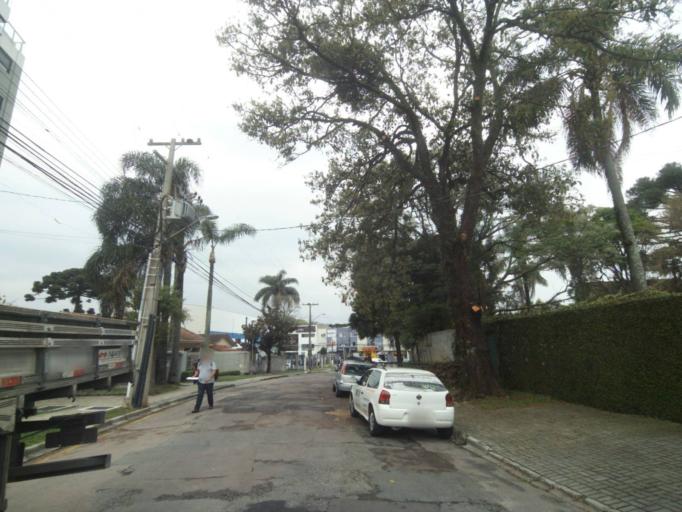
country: BR
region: Parana
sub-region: Curitiba
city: Curitiba
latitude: -25.4742
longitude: -49.2991
